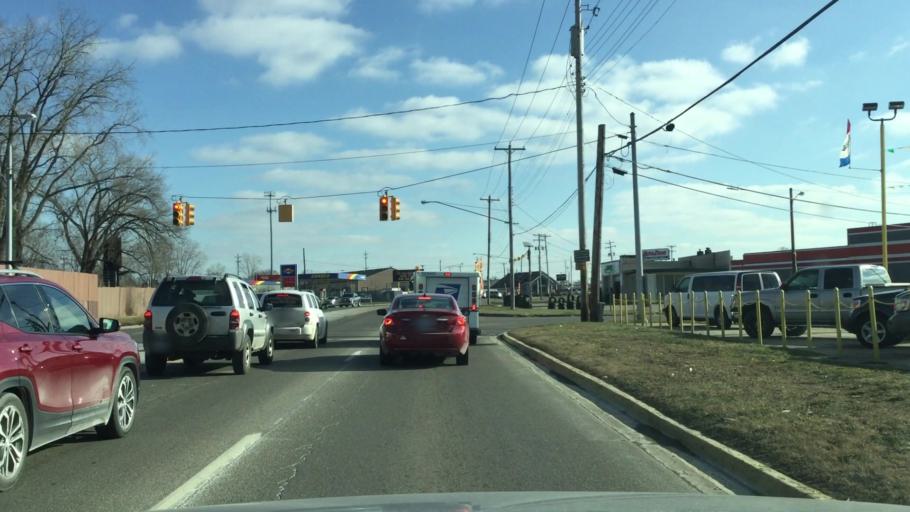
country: US
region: Michigan
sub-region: Genesee County
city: Flint
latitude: 43.0520
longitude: -83.6658
